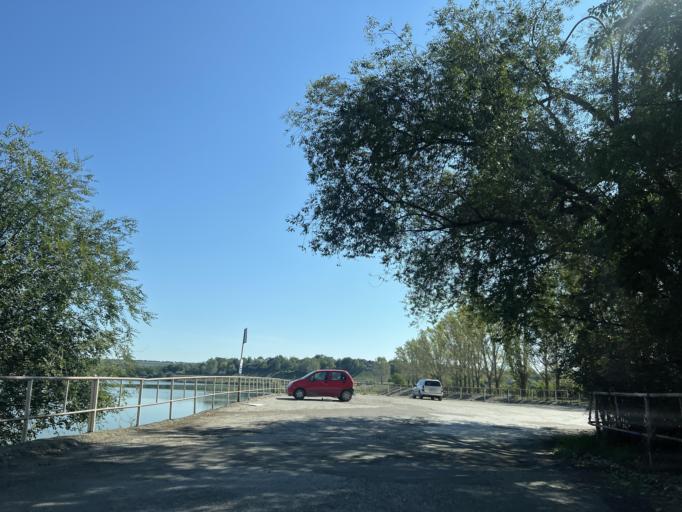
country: MD
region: Ungheni
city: Ungheni
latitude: 47.1997
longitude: 27.8000
